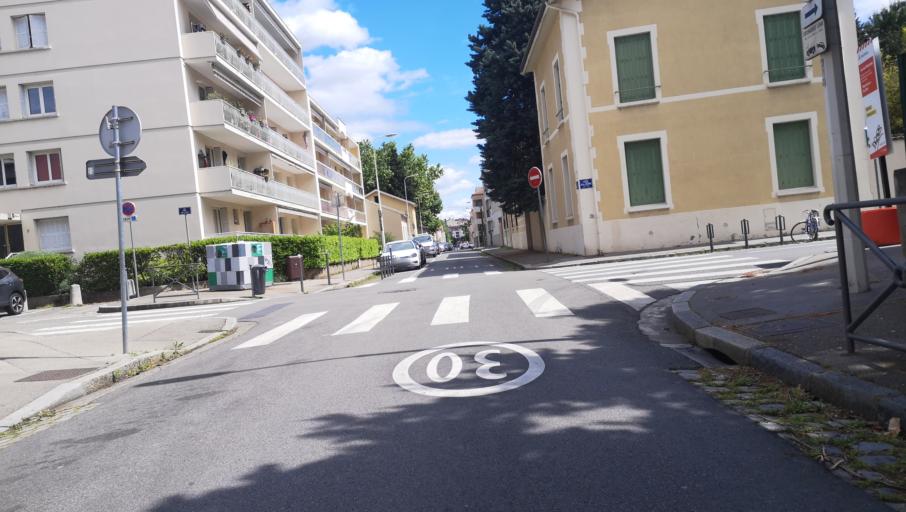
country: FR
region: Rhone-Alpes
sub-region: Departement du Rhone
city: Villeurbanne
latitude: 45.7516
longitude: 4.8776
